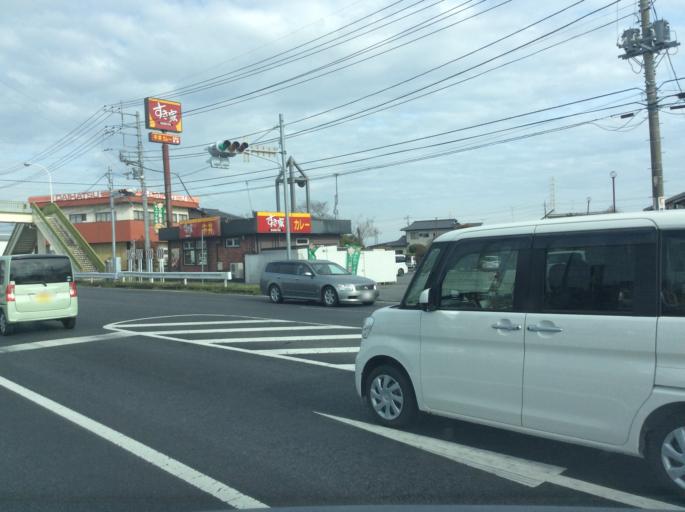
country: JP
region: Ibaraki
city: Ishige
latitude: 36.1798
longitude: 139.9685
